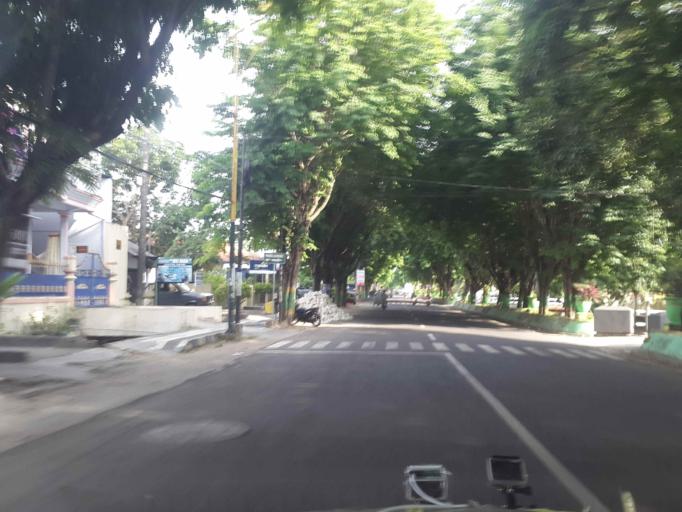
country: ID
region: East Java
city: Sumenep
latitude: -7.0161
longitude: 113.8719
